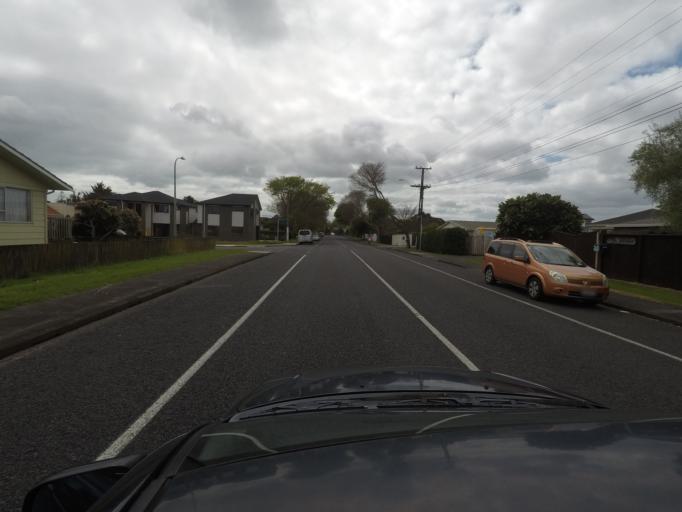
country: NZ
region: Auckland
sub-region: Auckland
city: Tamaki
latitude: -36.9369
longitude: 174.8586
